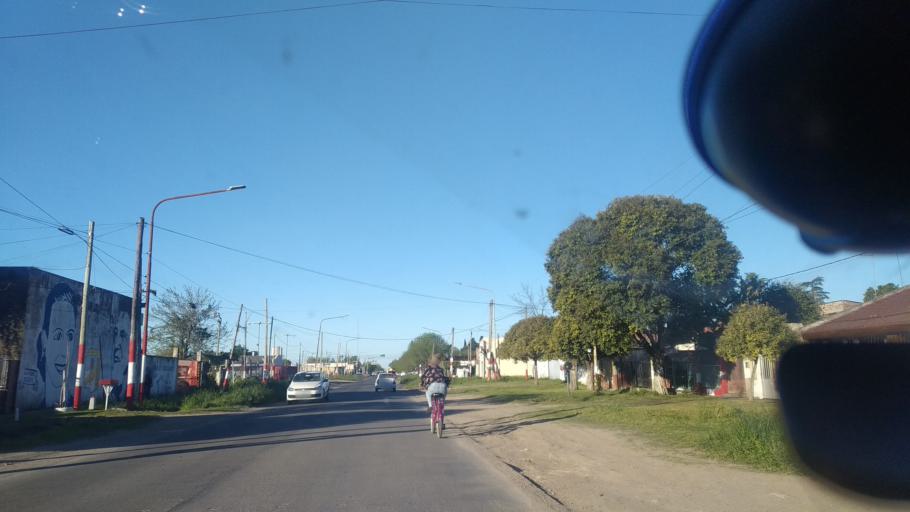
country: AR
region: Buenos Aires
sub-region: Partido de La Plata
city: La Plata
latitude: -34.9611
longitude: -57.9609
